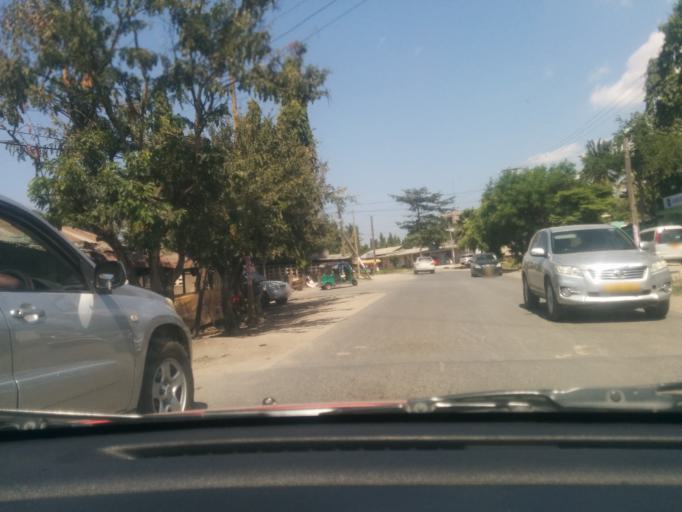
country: TZ
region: Dar es Salaam
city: Magomeni
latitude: -6.7717
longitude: 39.2240
